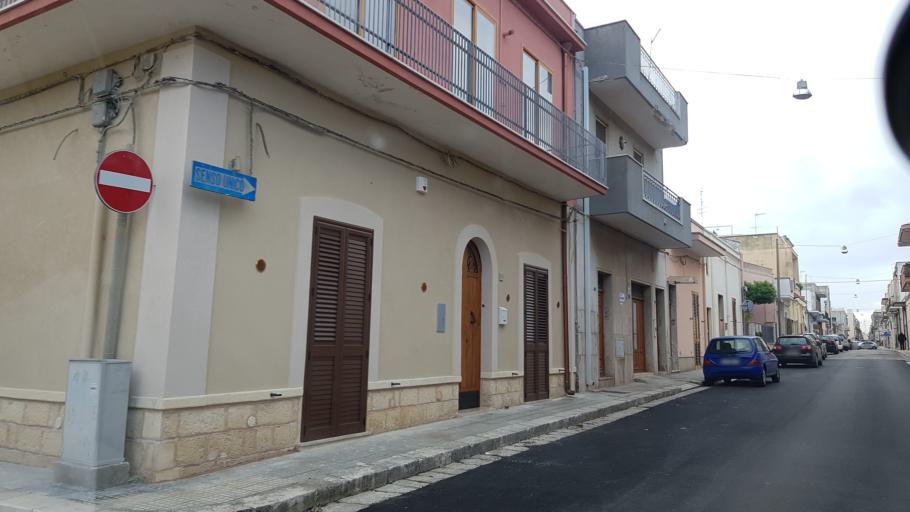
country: IT
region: Apulia
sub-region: Provincia di Brindisi
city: Mesagne
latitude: 40.5639
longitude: 17.8105
